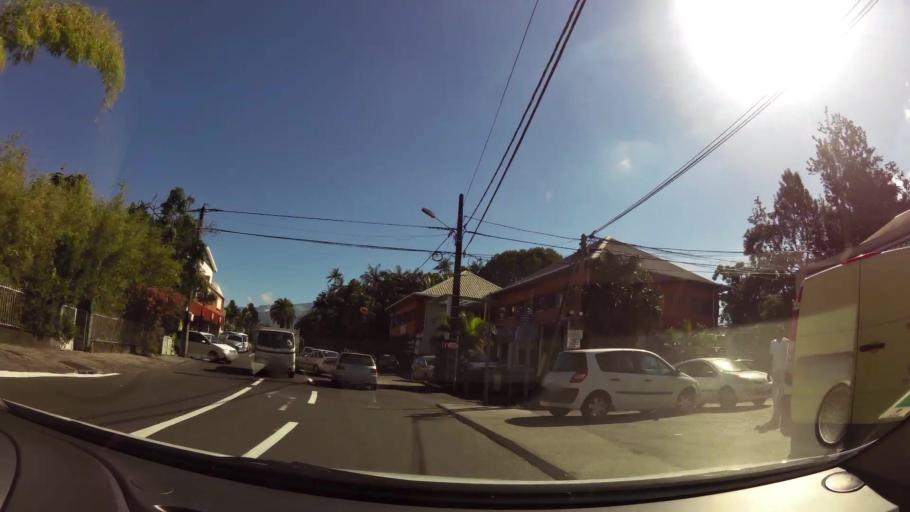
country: RE
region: Reunion
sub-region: Reunion
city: Le Tampon
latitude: -21.2617
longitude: 55.5050
